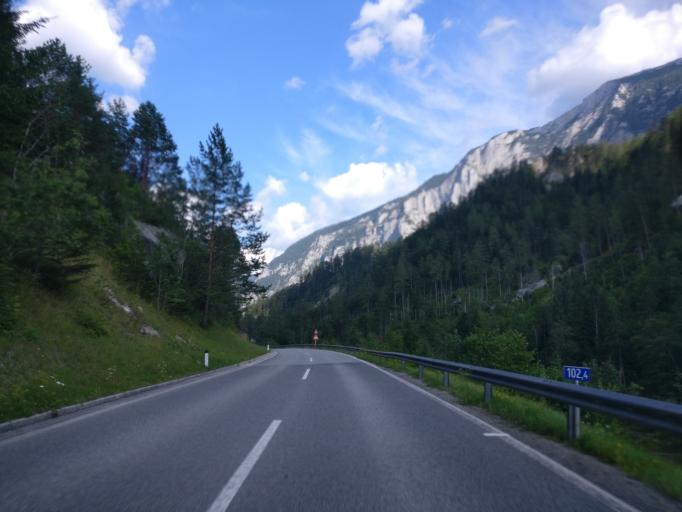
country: AT
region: Styria
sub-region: Politischer Bezirk Liezen
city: Johnsbach
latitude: 47.5904
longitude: 14.6392
